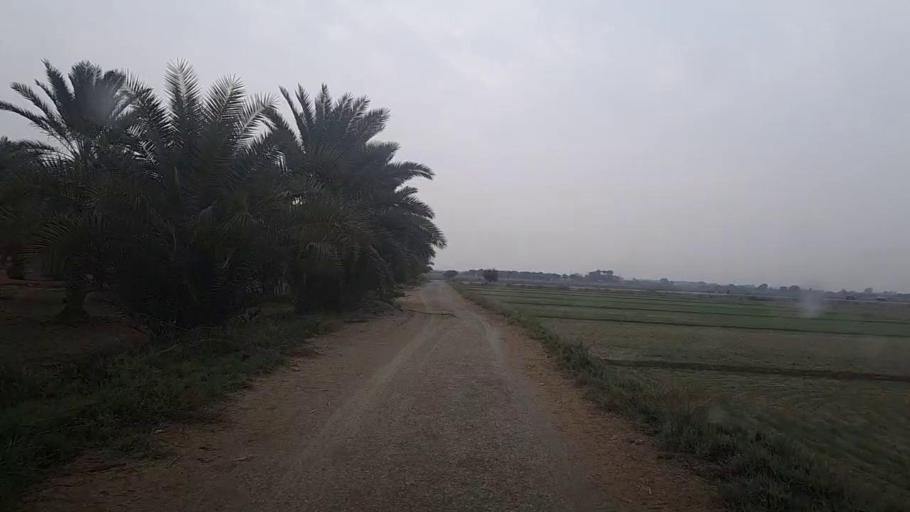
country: PK
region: Sindh
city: Gambat
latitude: 27.3633
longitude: 68.5818
